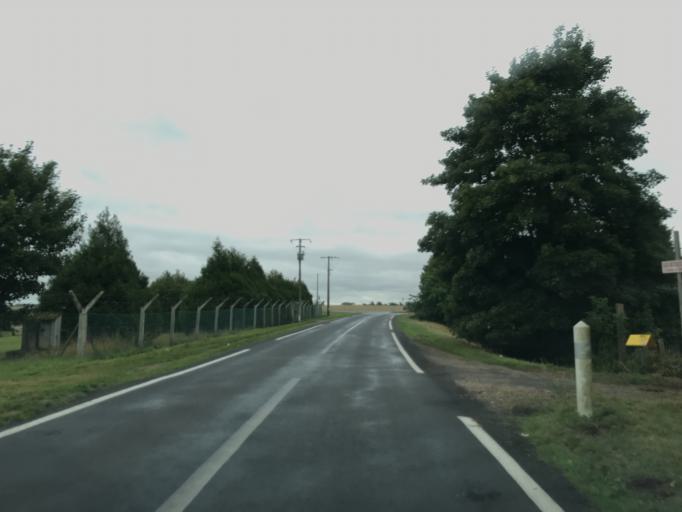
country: FR
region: Haute-Normandie
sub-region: Departement de l'Eure
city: Gravigny
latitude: 49.0153
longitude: 1.2453
